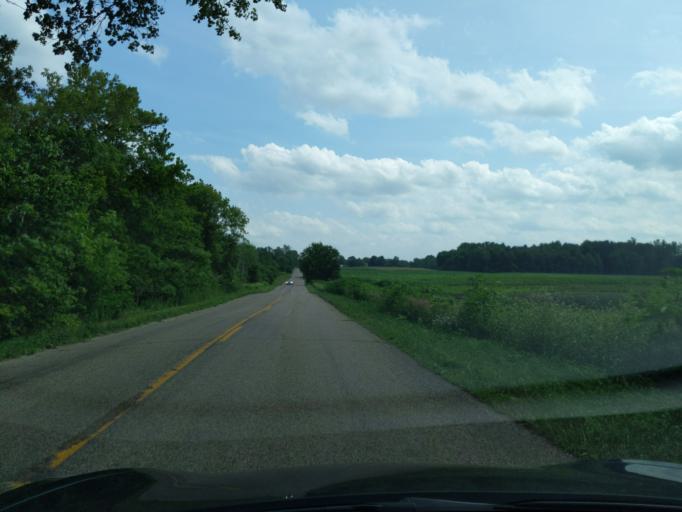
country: US
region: Michigan
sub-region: Eaton County
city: Eaton Rapids
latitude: 42.5497
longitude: -84.6019
